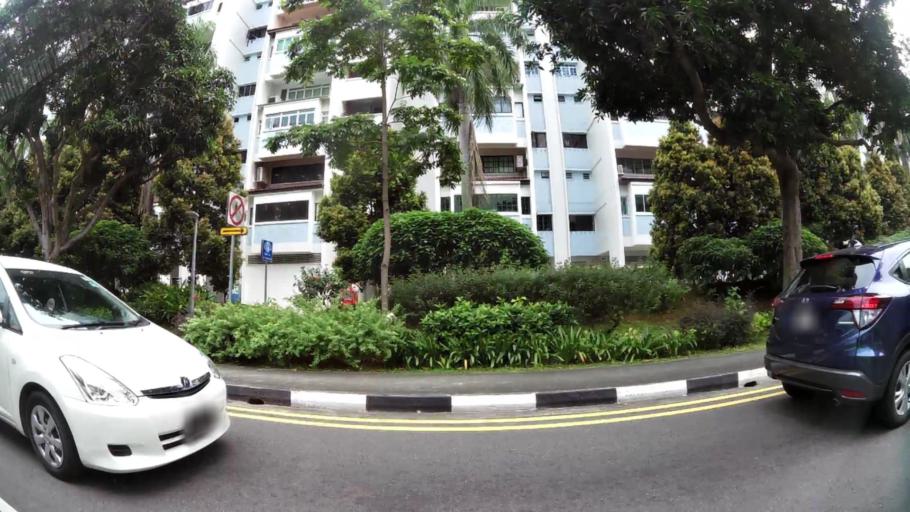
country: SG
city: Singapore
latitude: 1.3518
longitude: 103.9448
